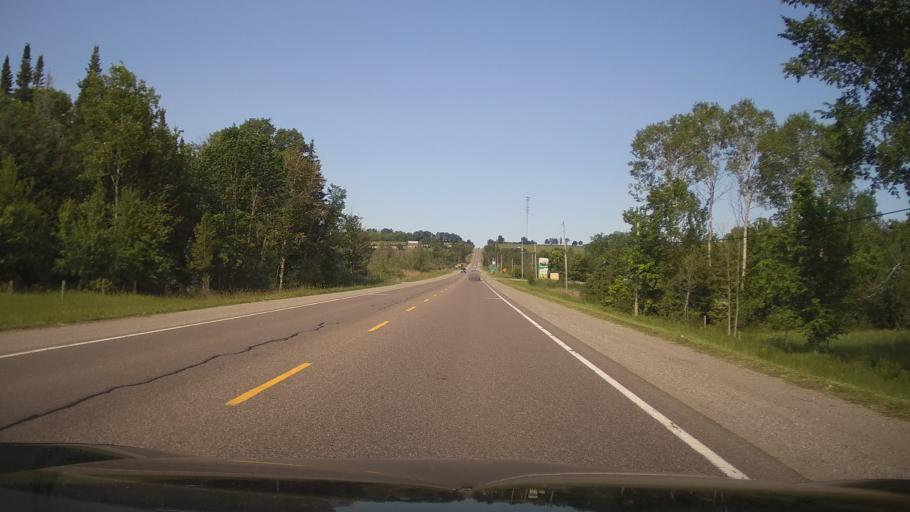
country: CA
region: Ontario
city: Omemee
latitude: 44.3207
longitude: -78.4708
